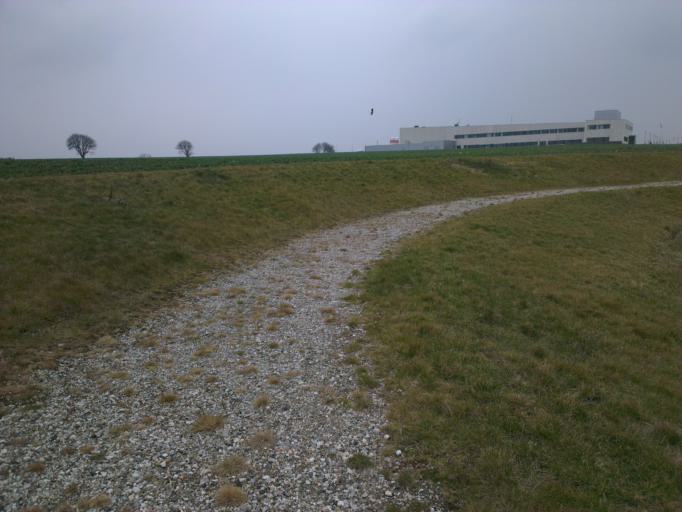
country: DK
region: Capital Region
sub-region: Frederikssund Kommune
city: Frederikssund
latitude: 55.8284
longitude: 12.1168
